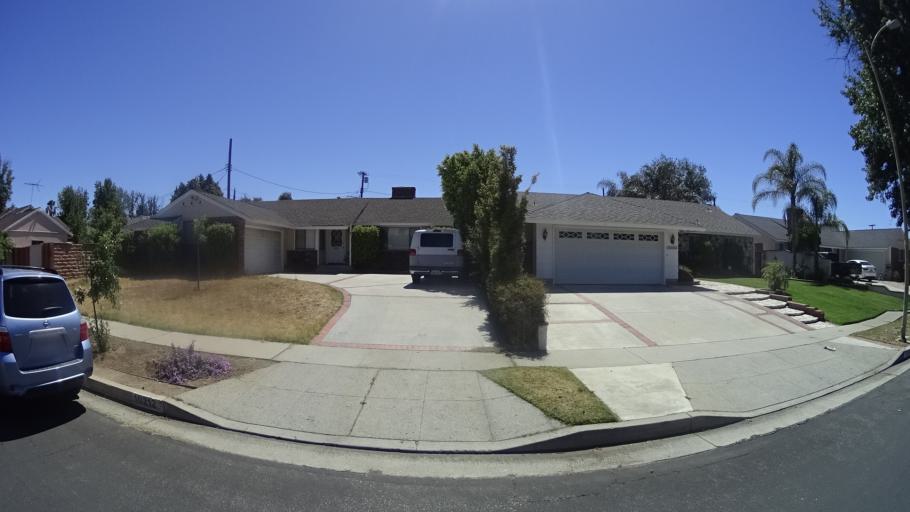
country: US
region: California
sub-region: Los Angeles County
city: San Fernando
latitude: 34.2557
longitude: -118.4610
